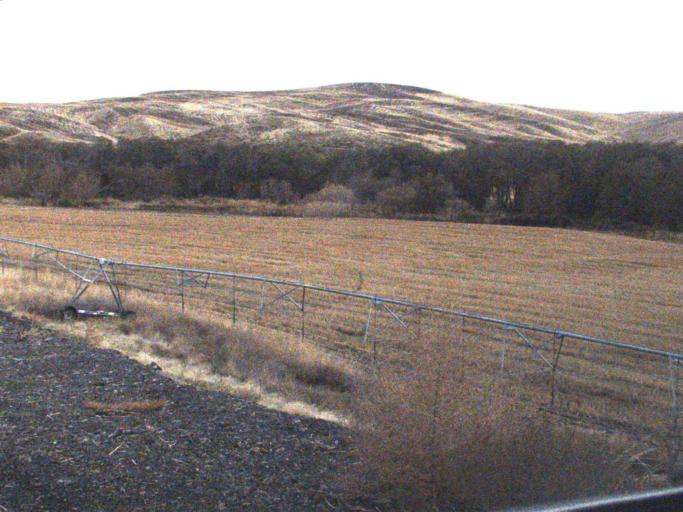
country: US
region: Washington
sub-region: Walla Walla County
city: Waitsburg
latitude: 46.5285
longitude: -118.1411
